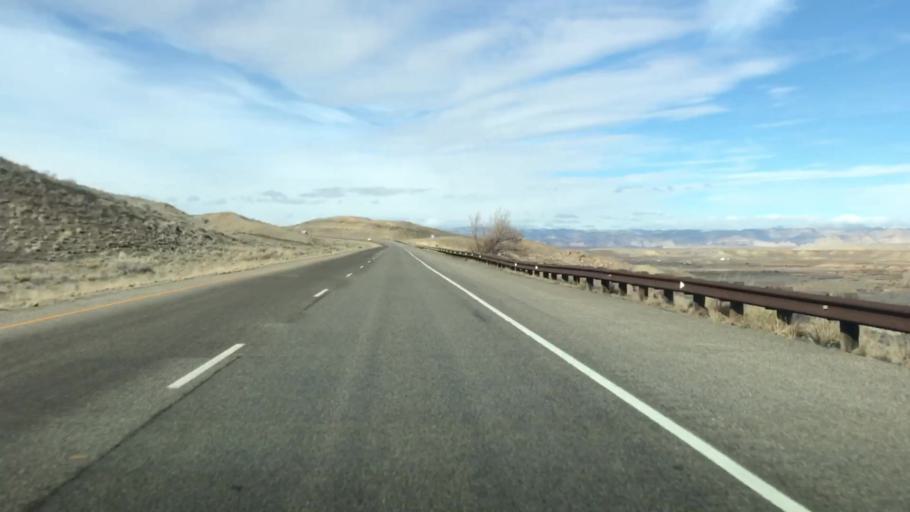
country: US
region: Colorado
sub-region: Mesa County
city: Loma
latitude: 39.2282
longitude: -108.8991
